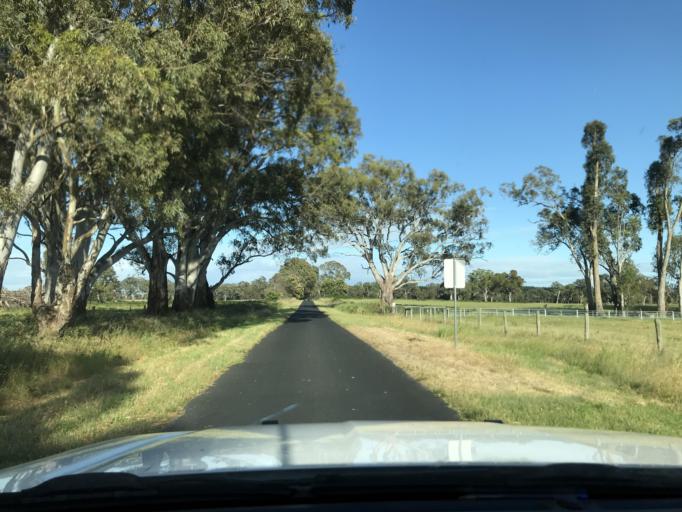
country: AU
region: South Australia
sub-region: Wattle Range
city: Penola
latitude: -37.2005
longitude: 140.9796
